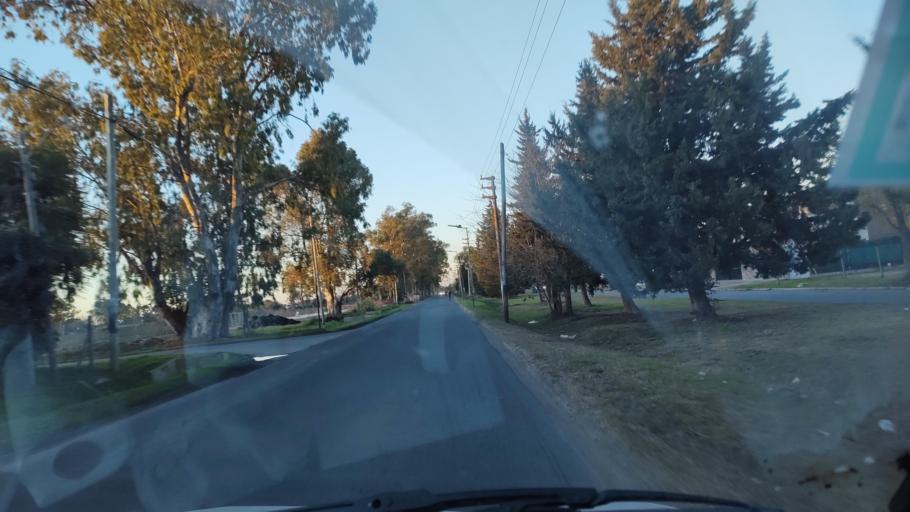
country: AR
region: Buenos Aires
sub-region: Partido de La Plata
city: La Plata
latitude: -34.9050
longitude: -58.0323
